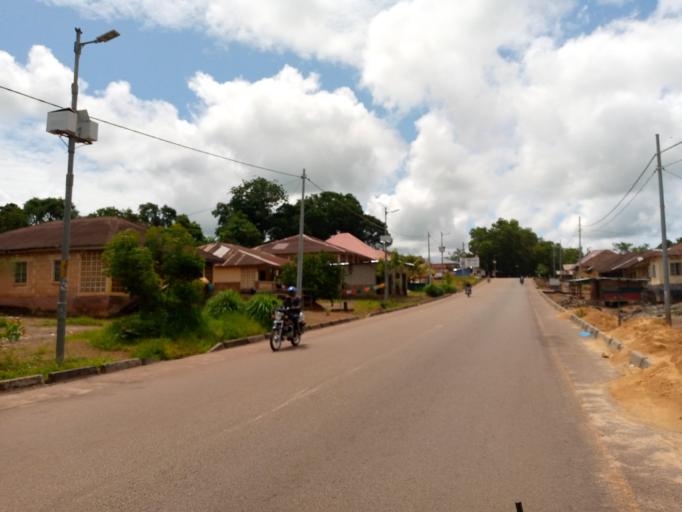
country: SL
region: Northern Province
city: Magburaka
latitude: 8.7207
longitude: -11.9412
